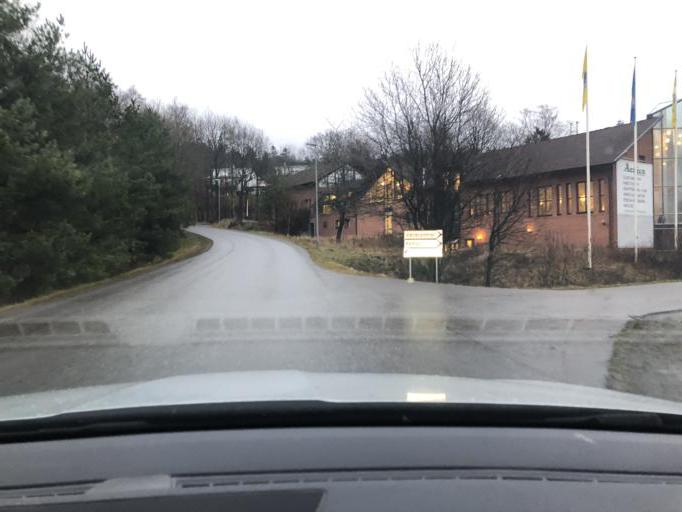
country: SE
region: Vaestra Goetaland
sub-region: Harryda Kommun
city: Landvetter
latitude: 57.6873
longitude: 12.1971
